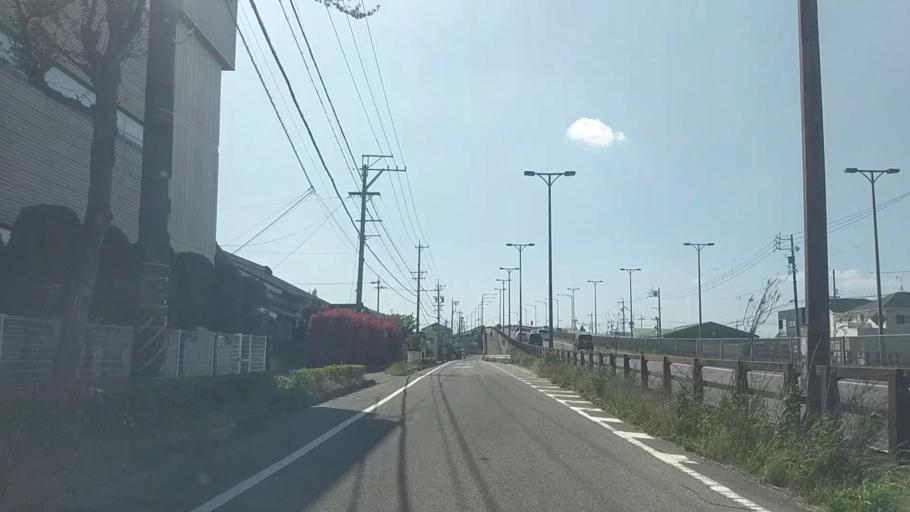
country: JP
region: Aichi
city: Okazaki
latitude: 34.9824
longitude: 137.1525
